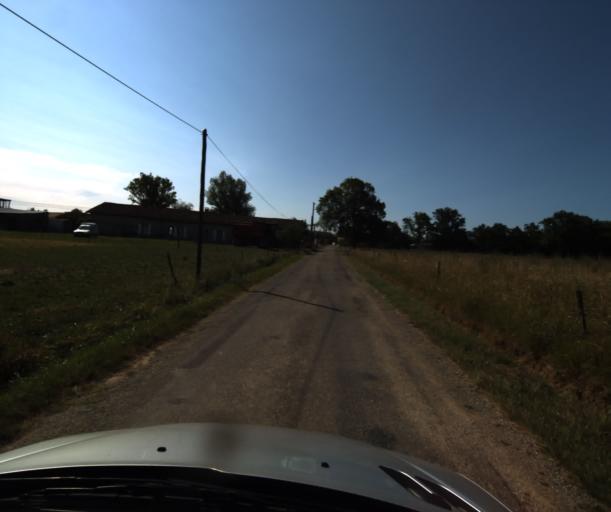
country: FR
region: Midi-Pyrenees
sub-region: Departement du Tarn-et-Garonne
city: Bressols
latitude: 43.9555
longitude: 1.2891
